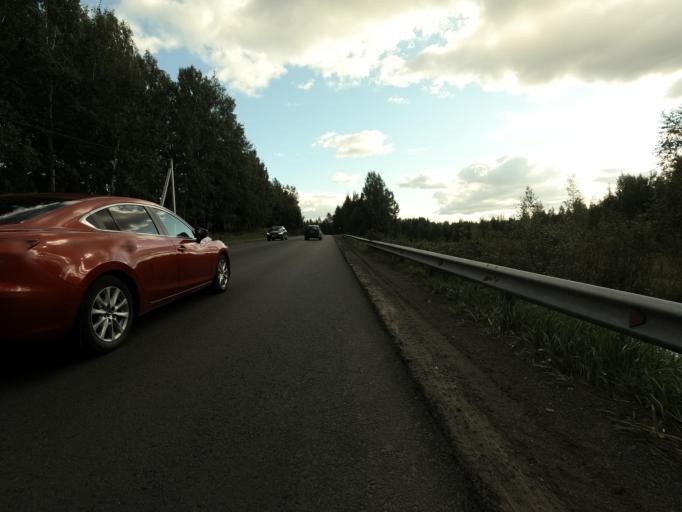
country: RU
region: Leningrad
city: Koltushi
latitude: 59.9732
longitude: 30.6532
